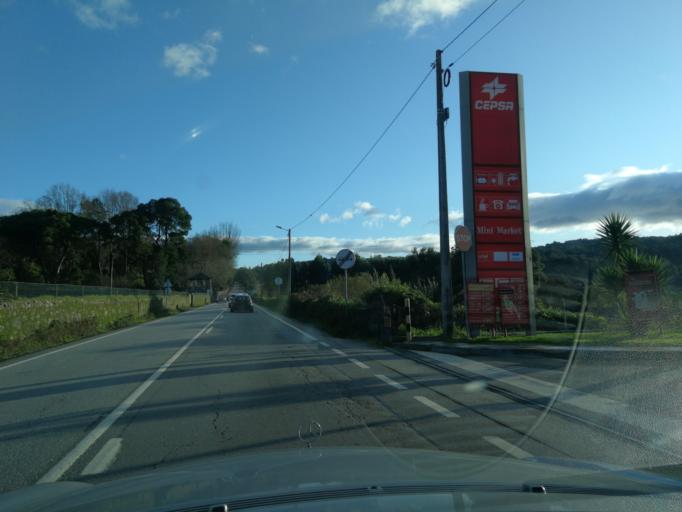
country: PT
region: Braga
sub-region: Esposende
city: Marinhas
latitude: 41.6030
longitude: -8.7409
